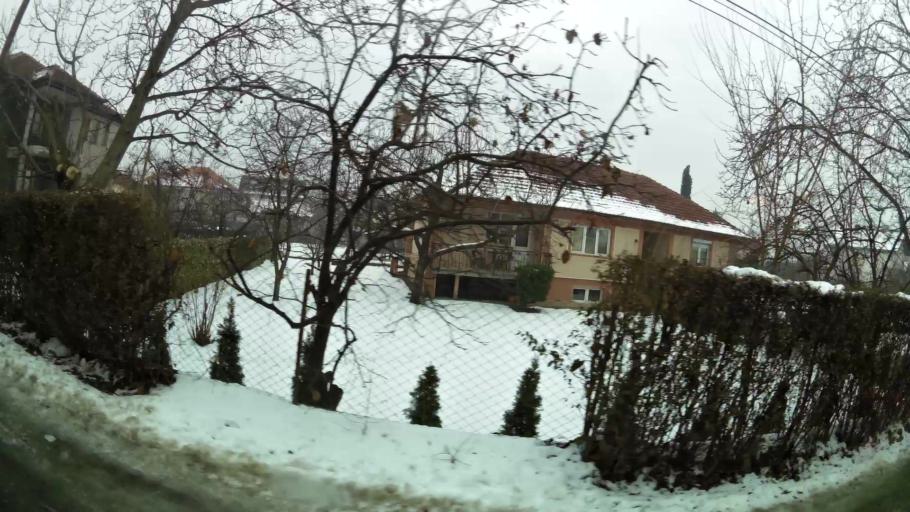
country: MK
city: Kondovo
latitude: 42.0442
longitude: 21.3502
